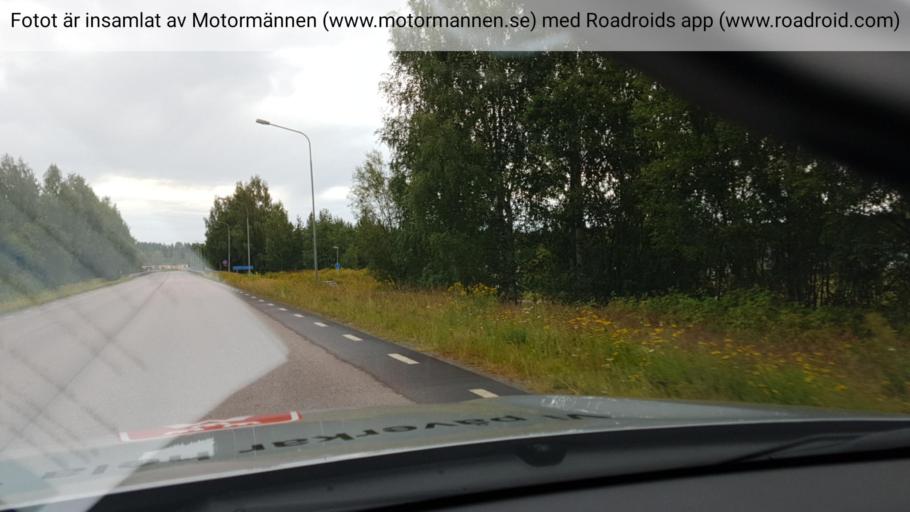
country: SE
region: Norrbotten
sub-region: Bodens Kommun
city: Boden
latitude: 65.8249
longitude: 21.6187
